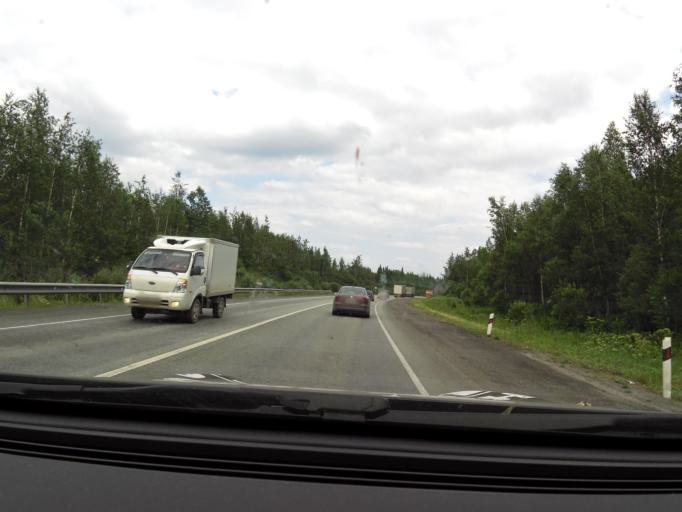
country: RU
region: Sverdlovsk
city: Bilimbay
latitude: 56.8589
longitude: 59.7565
